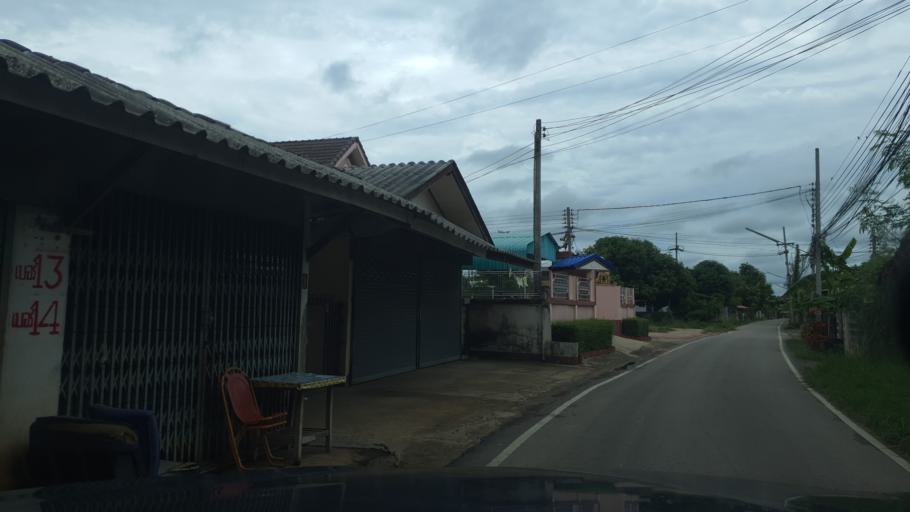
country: TH
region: Lampang
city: Hang Chat
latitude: 18.3091
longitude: 99.3594
